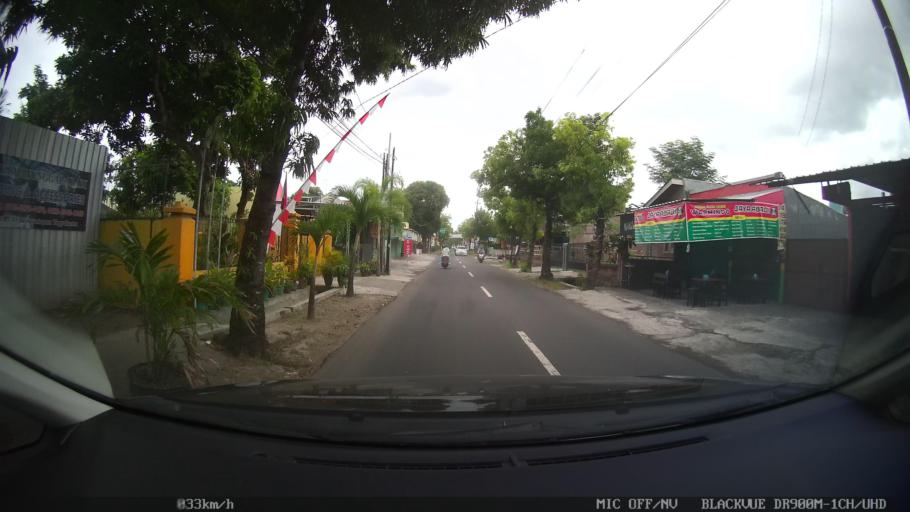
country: ID
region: Daerah Istimewa Yogyakarta
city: Depok
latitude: -7.8206
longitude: 110.4154
